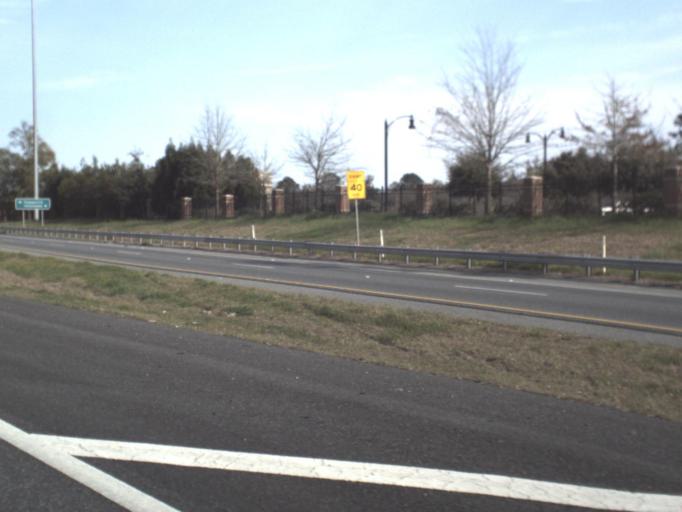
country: US
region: Florida
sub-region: Leon County
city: Tallahassee
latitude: 30.5012
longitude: -84.2576
